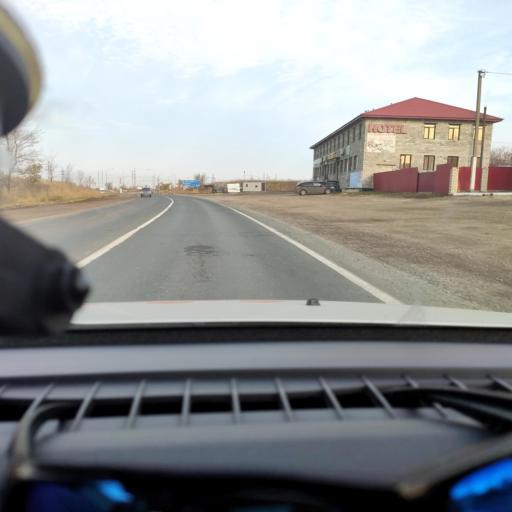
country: RU
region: Samara
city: Chapayevsk
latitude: 52.9944
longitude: 49.7681
